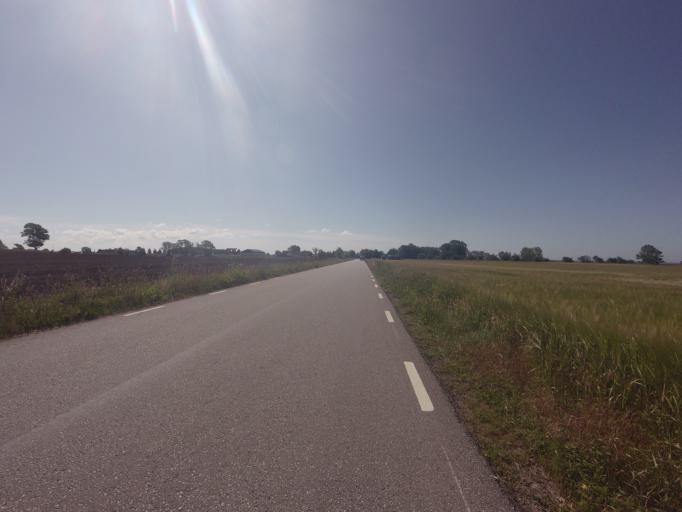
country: SE
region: Skane
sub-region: Malmo
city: Bunkeflostrand
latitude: 55.5131
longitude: 12.9363
